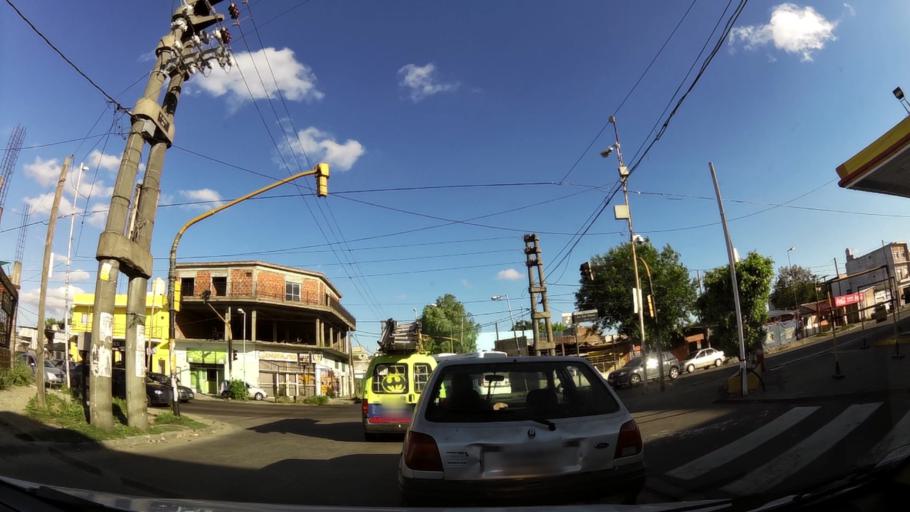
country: AR
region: Buenos Aires
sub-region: Partido de Moron
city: Moron
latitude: -34.6832
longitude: -58.6196
